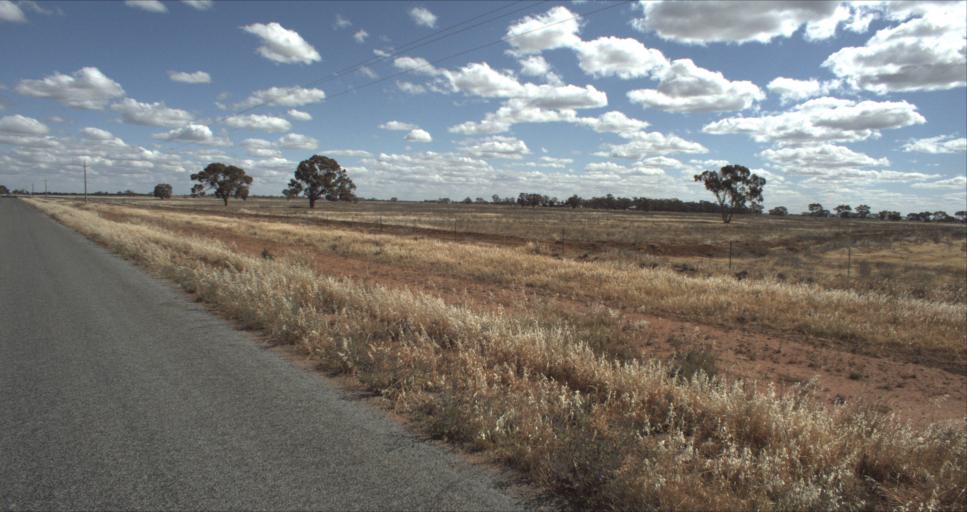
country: AU
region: New South Wales
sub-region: Leeton
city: Leeton
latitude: -34.4611
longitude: 146.2527
